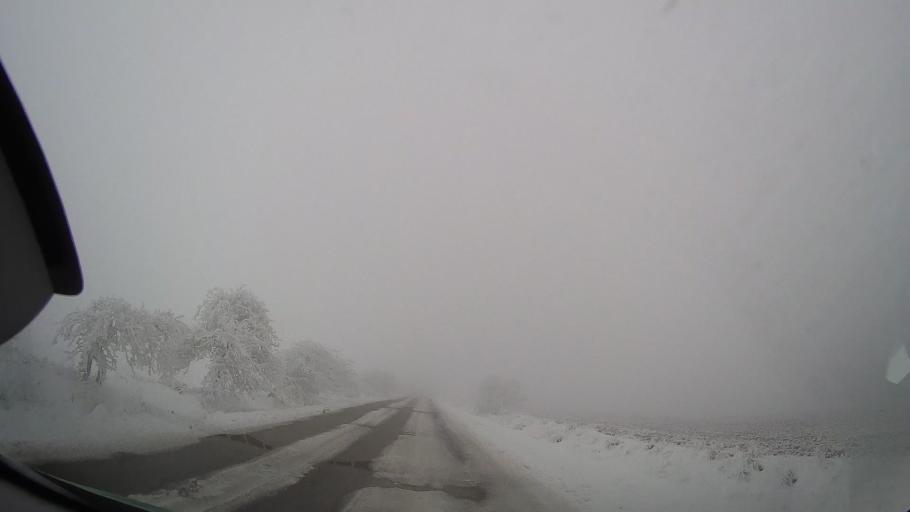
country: RO
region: Neamt
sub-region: Comuna Valea Ursului
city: Valea Ursului
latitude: 46.8237
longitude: 27.0628
